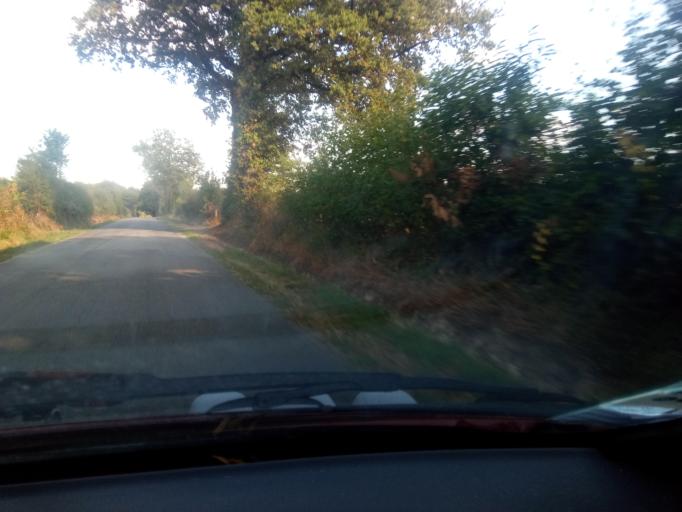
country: FR
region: Poitou-Charentes
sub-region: Departement de la Vienne
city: Availles-Limouzine
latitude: 46.1292
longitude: 0.7126
